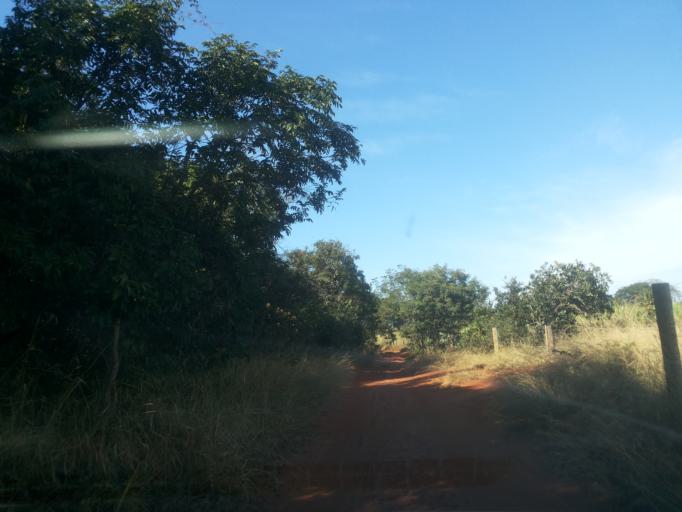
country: BR
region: Minas Gerais
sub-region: Ituiutaba
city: Ituiutaba
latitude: -19.1223
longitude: -49.3818
